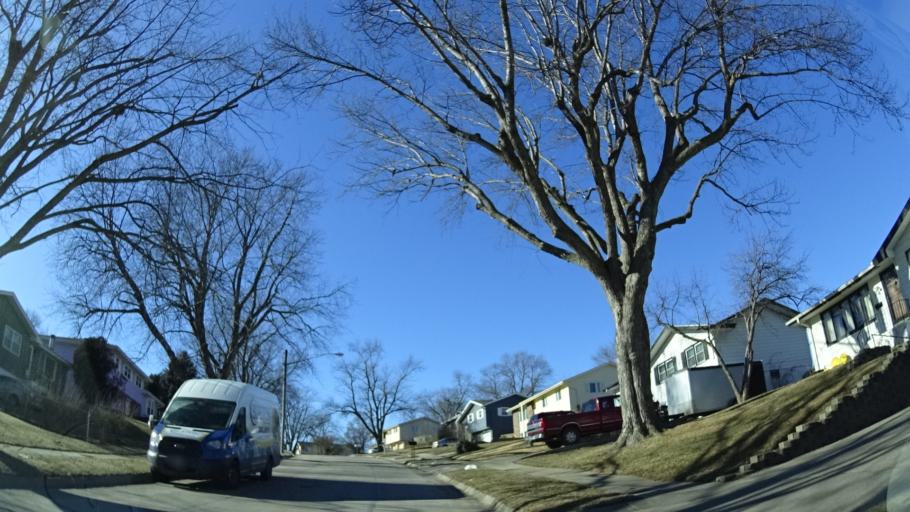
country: US
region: Nebraska
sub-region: Sarpy County
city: Offutt Air Force Base
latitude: 41.1485
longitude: -95.9236
